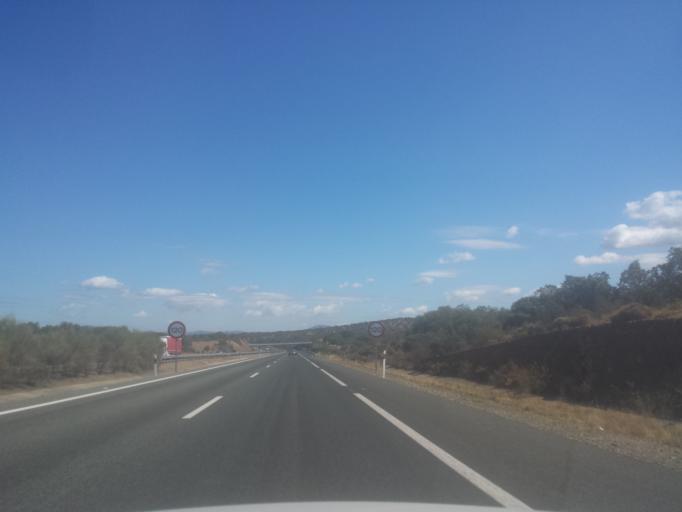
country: ES
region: Andalusia
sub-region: Provincia de Huelva
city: Santa Olalla del Cala
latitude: 37.8515
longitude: -6.2186
